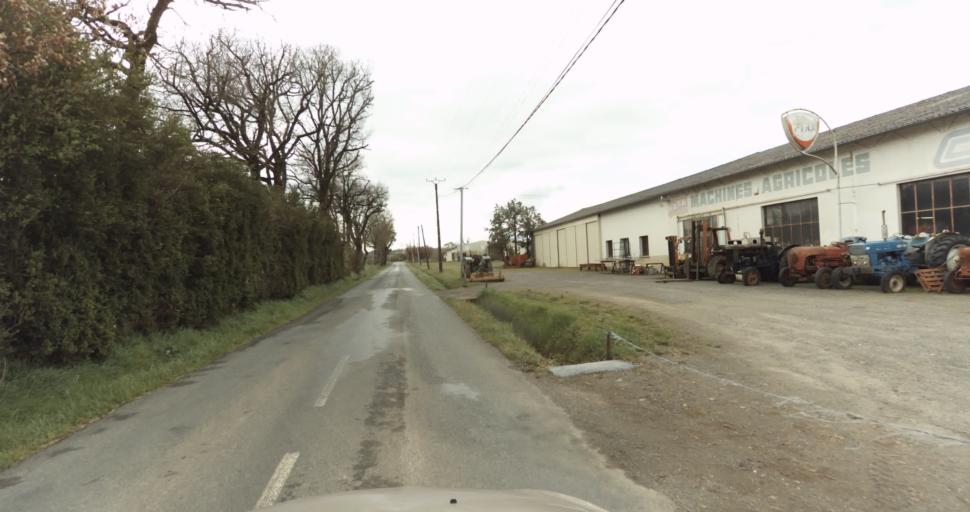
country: FR
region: Midi-Pyrenees
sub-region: Departement du Tarn
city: Puygouzon
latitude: 43.8903
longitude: 2.1923
